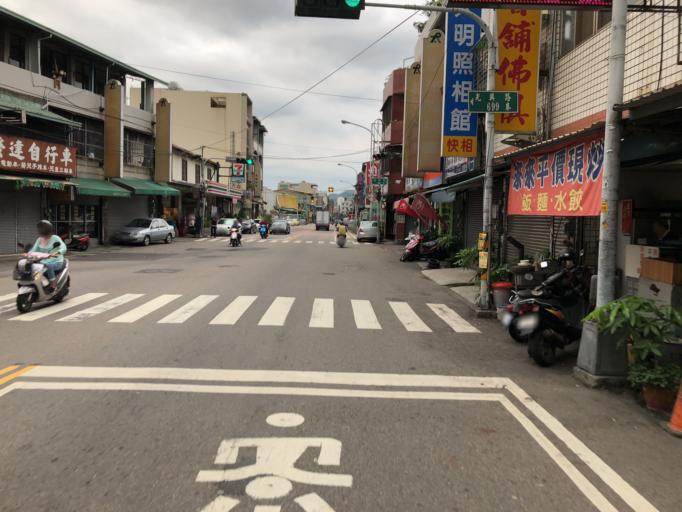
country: TW
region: Taiwan
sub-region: Taichung City
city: Taichung
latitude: 24.1086
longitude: 120.7297
